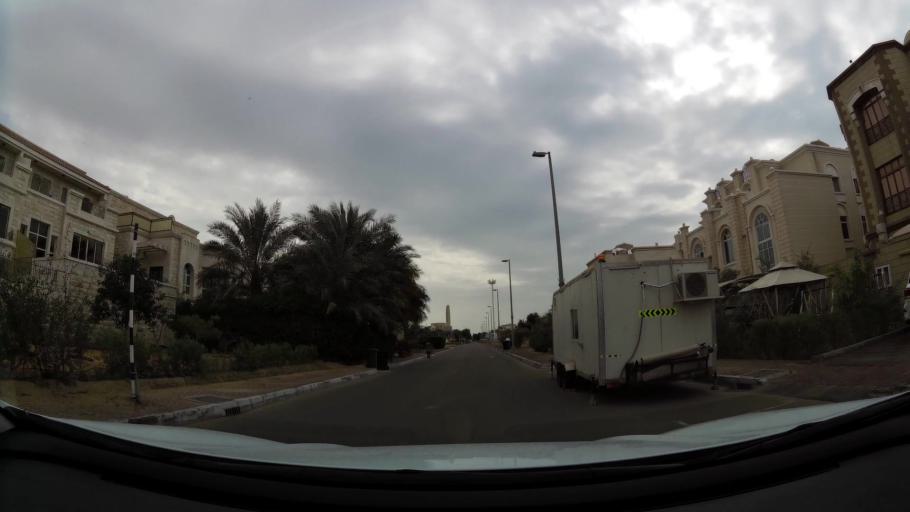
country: AE
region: Abu Dhabi
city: Abu Dhabi
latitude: 24.4317
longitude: 54.4095
